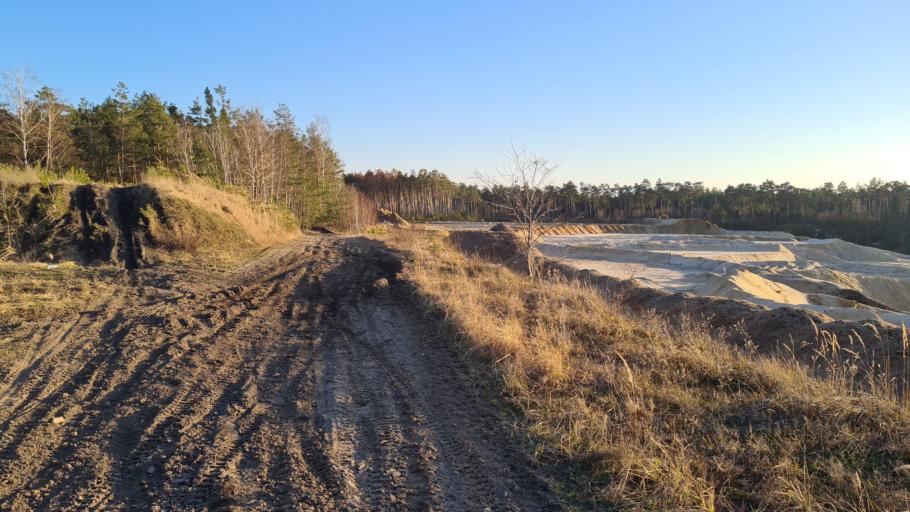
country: DE
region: Brandenburg
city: Finsterwalde
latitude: 51.6366
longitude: 13.6595
